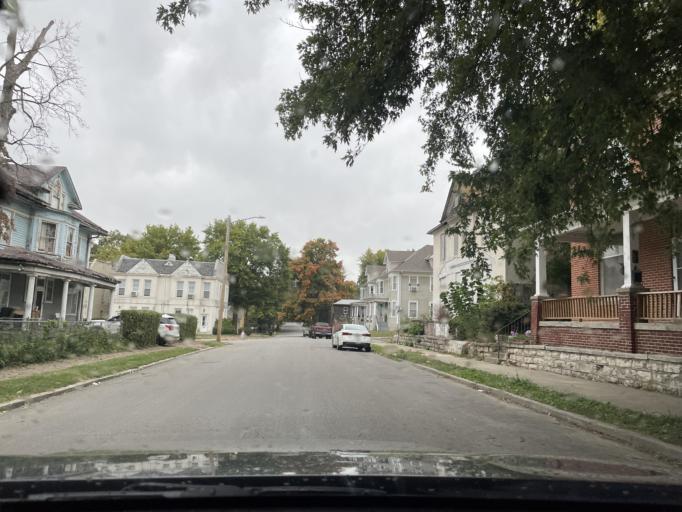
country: US
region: Missouri
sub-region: Buchanan County
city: Saint Joseph
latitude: 39.7731
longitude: -94.8467
